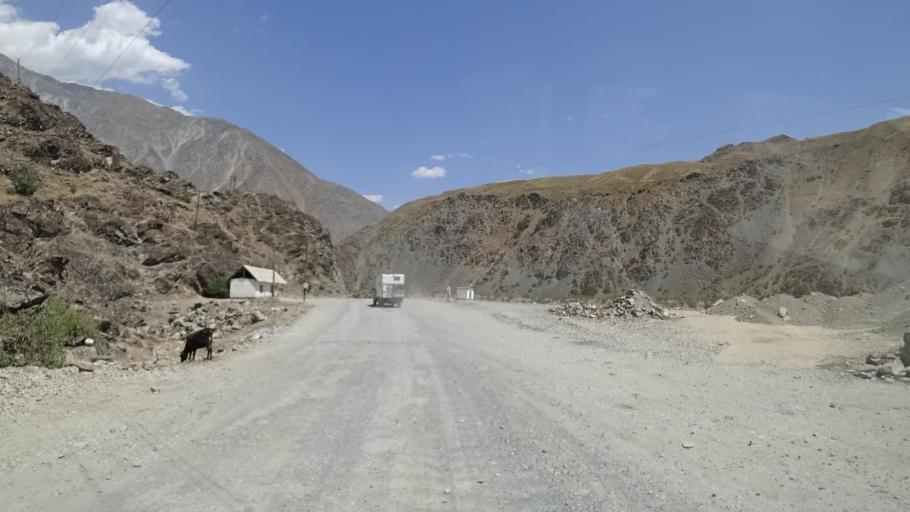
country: AF
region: Badakhshan
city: Nusay
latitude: 38.4640
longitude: 70.8645
